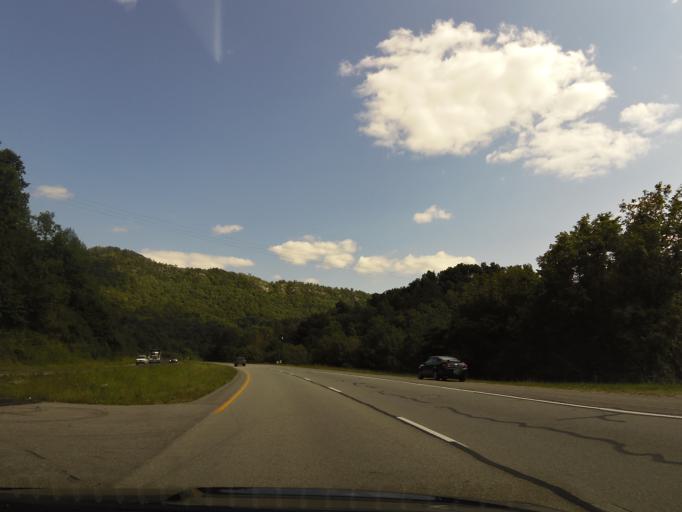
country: US
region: Kentucky
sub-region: Bell County
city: Pineville
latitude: 36.6976
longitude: -83.6911
